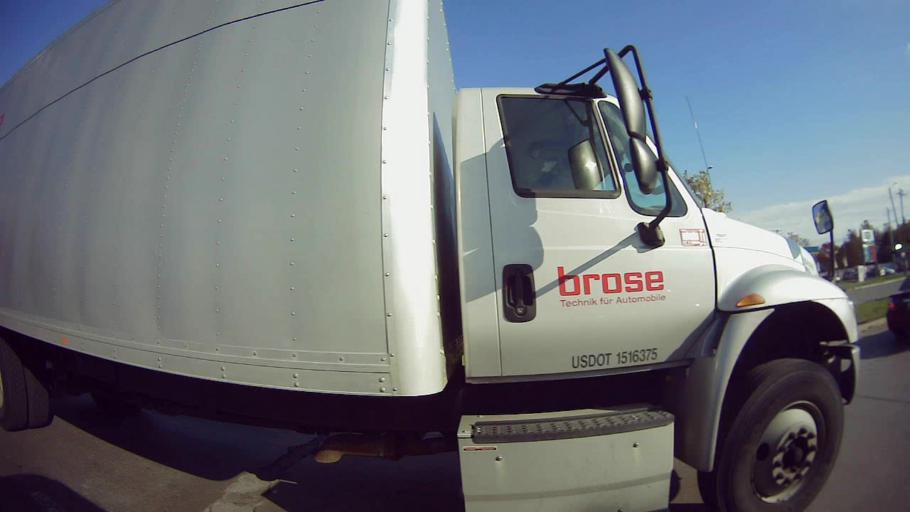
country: US
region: Michigan
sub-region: Macomb County
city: Warren
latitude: 42.4348
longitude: -83.0146
